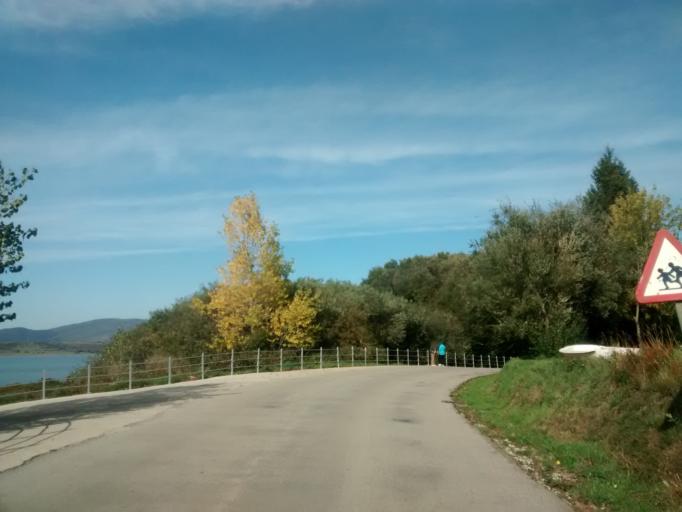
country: ES
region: Castille and Leon
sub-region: Provincia de Burgos
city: Arija
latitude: 42.9889
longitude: -3.9523
